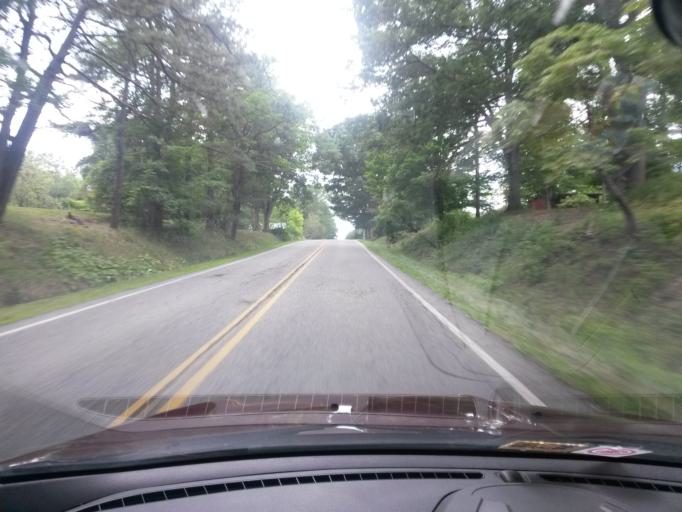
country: US
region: Virginia
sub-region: Highland County
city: Monterey
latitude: 38.4580
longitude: -79.5285
